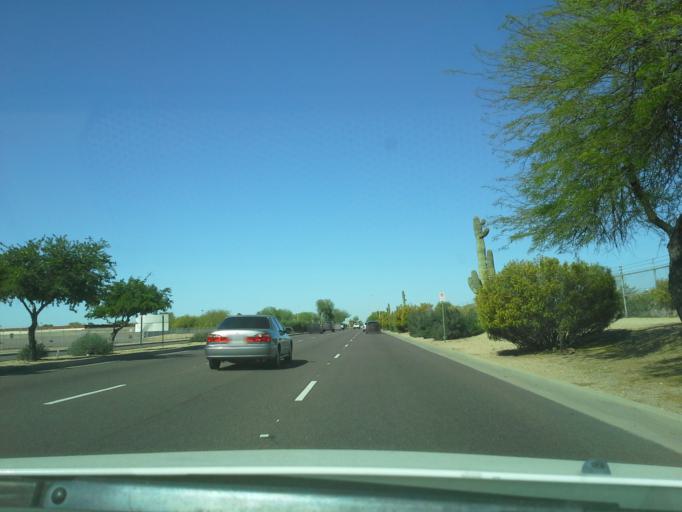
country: US
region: Arizona
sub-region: Maricopa County
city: Paradise Valley
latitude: 33.6327
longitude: -111.8988
